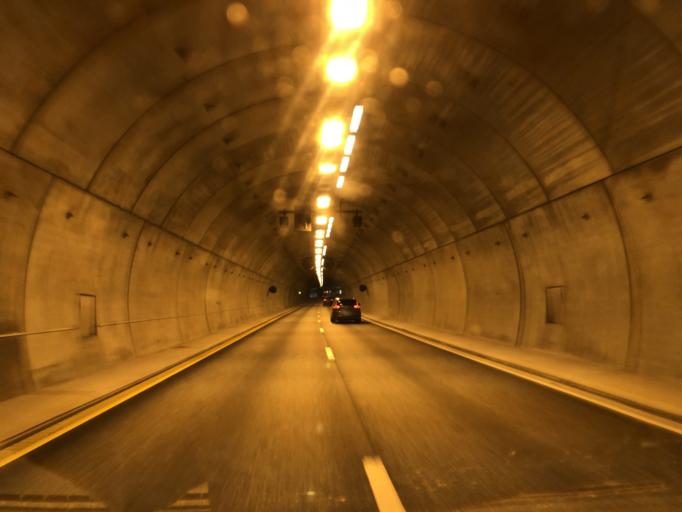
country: NO
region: Akershus
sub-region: Eidsvoll
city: Eidsvoll
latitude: 60.4384
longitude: 11.2416
